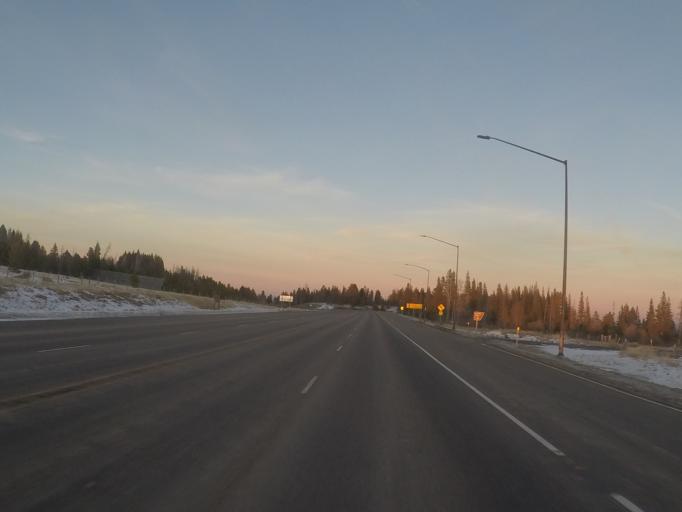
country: US
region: Montana
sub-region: Lewis and Clark County
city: Helena West Side
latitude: 46.5612
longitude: -112.3095
